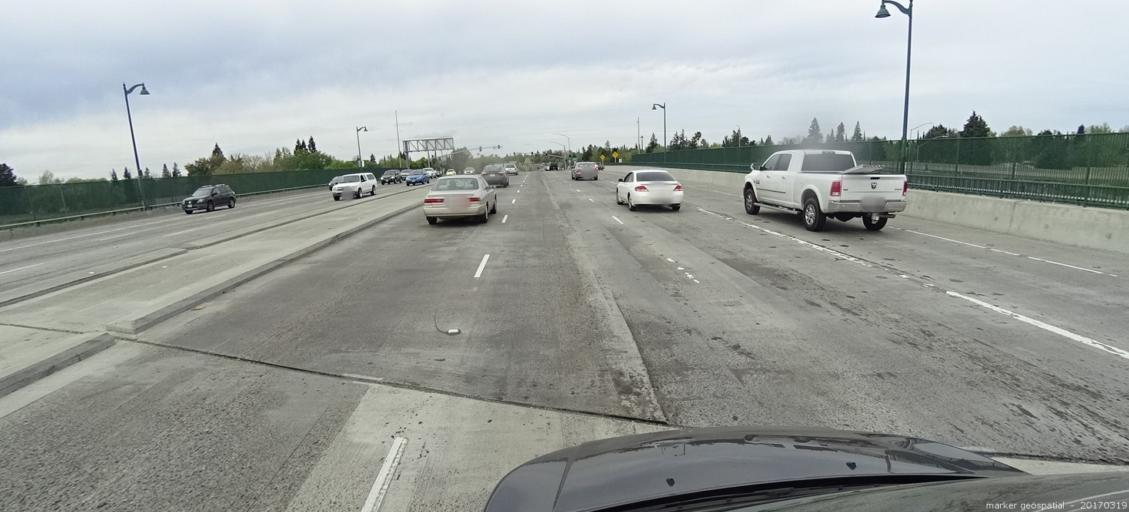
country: US
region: California
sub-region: Sacramento County
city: Rosemont
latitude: 38.5583
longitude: -121.3790
